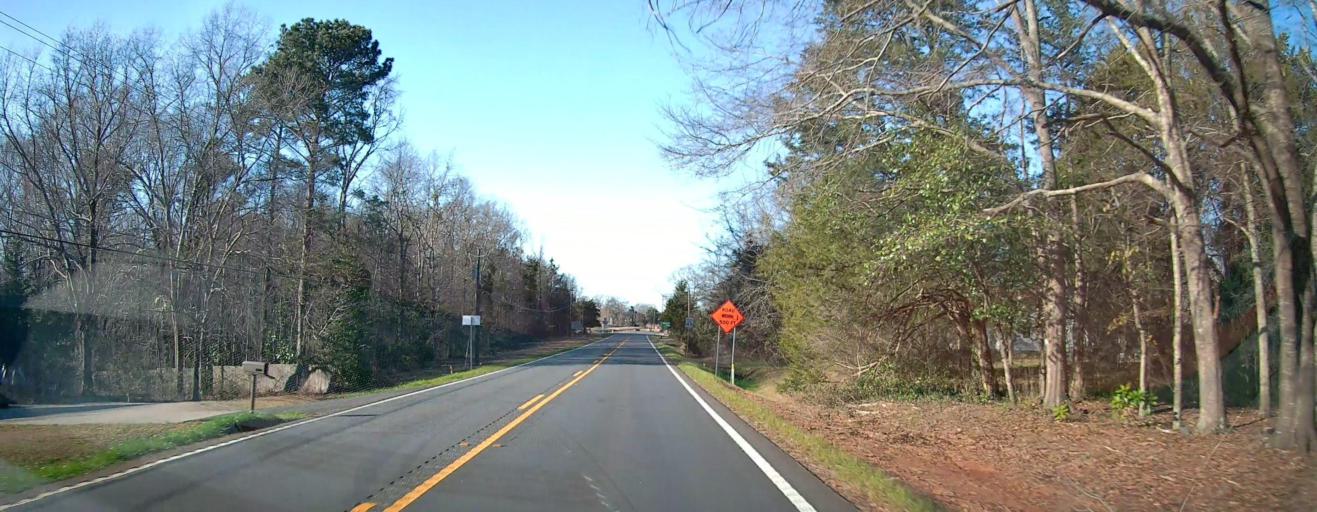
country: US
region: Georgia
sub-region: Talbot County
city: Sardis
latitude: 32.8029
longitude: -84.6950
